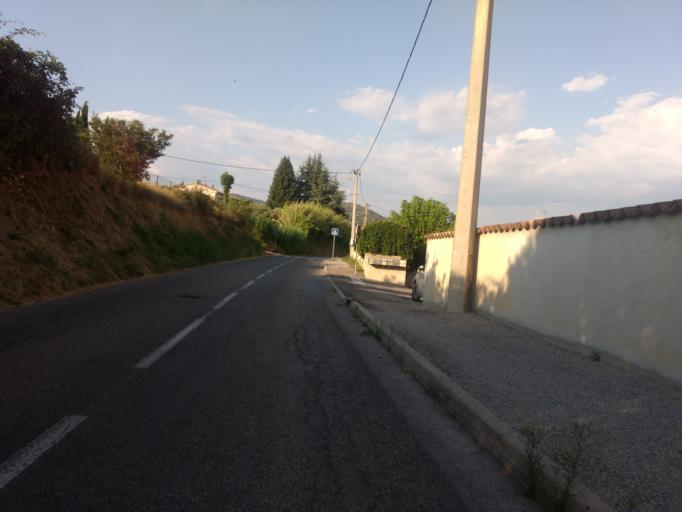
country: FR
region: Provence-Alpes-Cote d'Azur
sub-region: Departement des Alpes-de-Haute-Provence
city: Manosque
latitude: 43.8217
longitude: 5.7787
